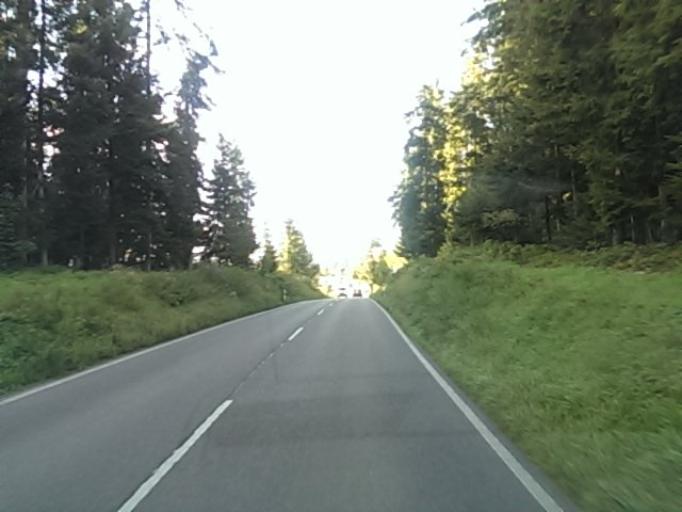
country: DE
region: Baden-Wuerttemberg
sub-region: Freiburg Region
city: Dornhan
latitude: 48.3167
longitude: 8.4718
